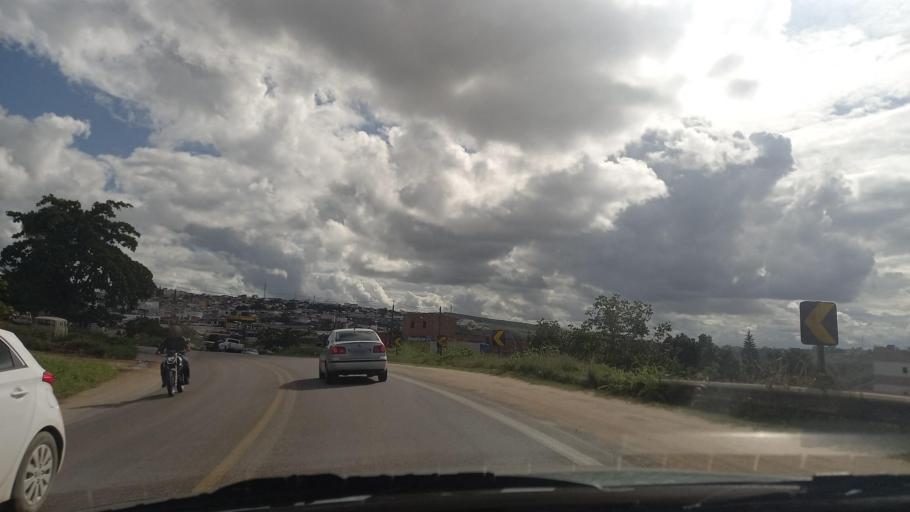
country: BR
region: Pernambuco
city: Garanhuns
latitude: -8.8781
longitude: -36.4822
